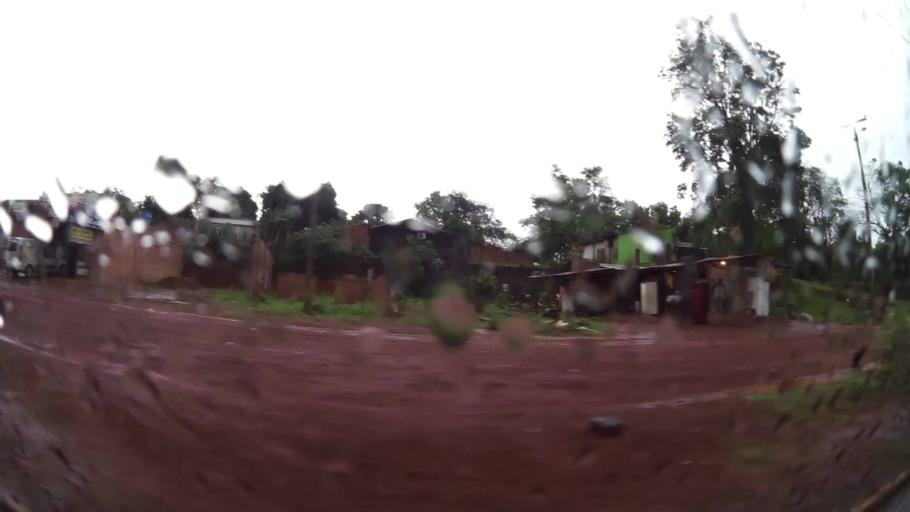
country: PY
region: Alto Parana
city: Presidente Franco
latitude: -25.5250
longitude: -54.6775
